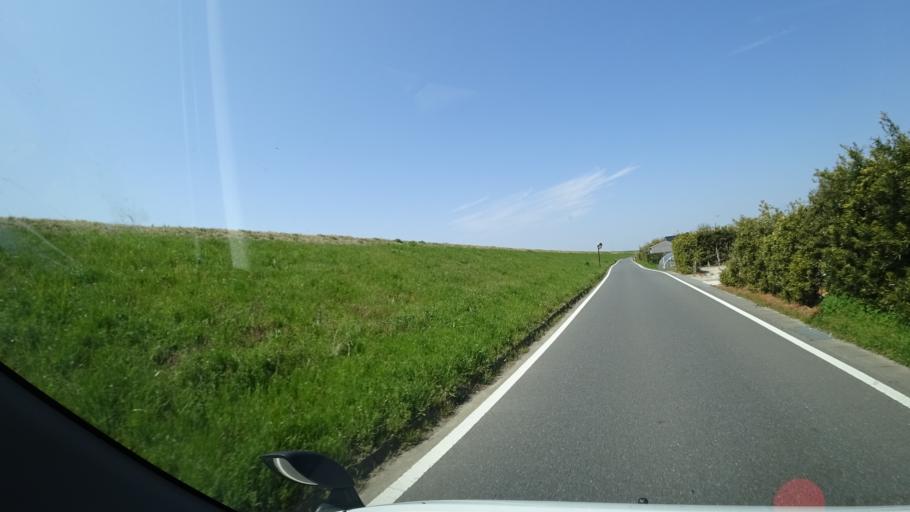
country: JP
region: Ibaraki
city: Edosaki
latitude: 35.8689
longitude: 140.2999
